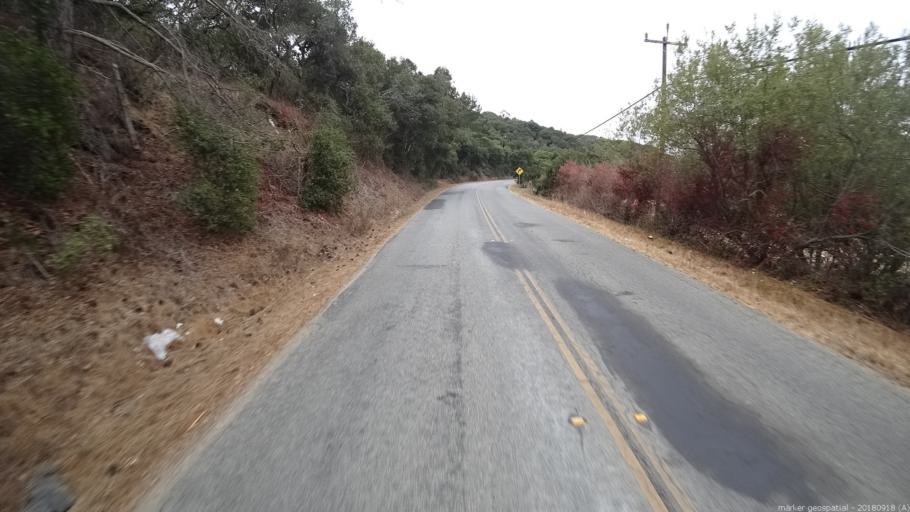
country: US
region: California
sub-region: Monterey County
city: Prunedale
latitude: 36.7789
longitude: -121.6431
